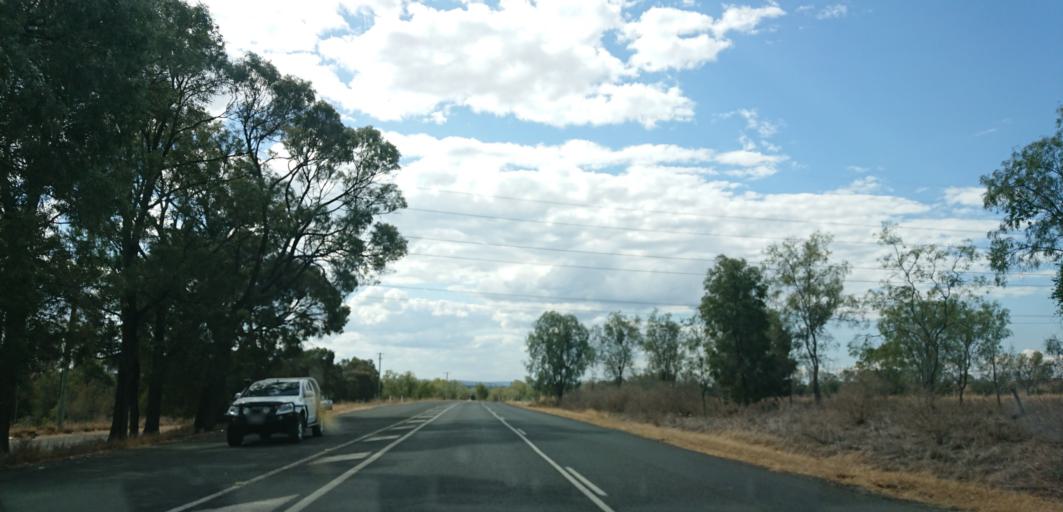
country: AU
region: Queensland
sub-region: Lockyer Valley
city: Gatton
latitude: -27.6373
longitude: 152.1855
